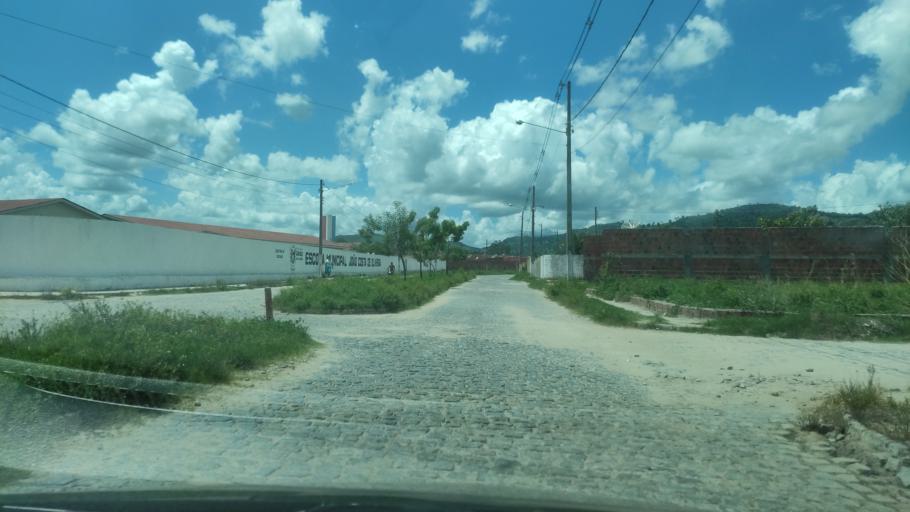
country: BR
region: Alagoas
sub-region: Uniao Dos Palmares
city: Uniao dos Palmares
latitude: -9.1467
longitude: -36.0023
